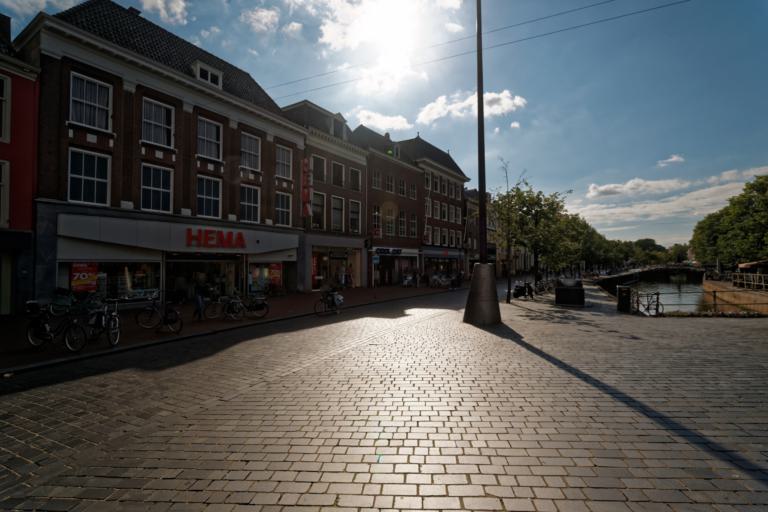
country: NL
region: Friesland
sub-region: Gemeente Leeuwarden
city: Leeuwarden
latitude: 53.2006
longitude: 5.7949
